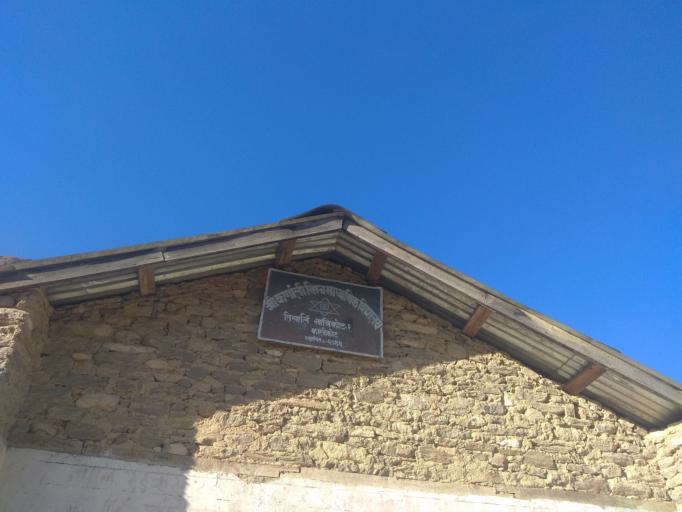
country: NP
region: Mid Western
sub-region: Bheri Zone
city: Dailekh
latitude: 29.2603
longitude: 81.6797
